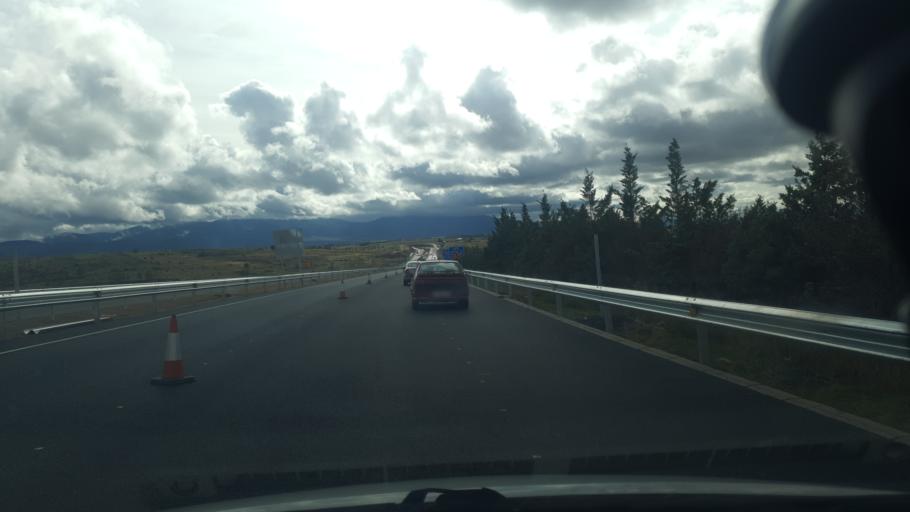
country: ES
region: Castille and Leon
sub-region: Provincia de Segovia
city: San Cristobal de Segovia
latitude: 40.9675
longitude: -4.0857
